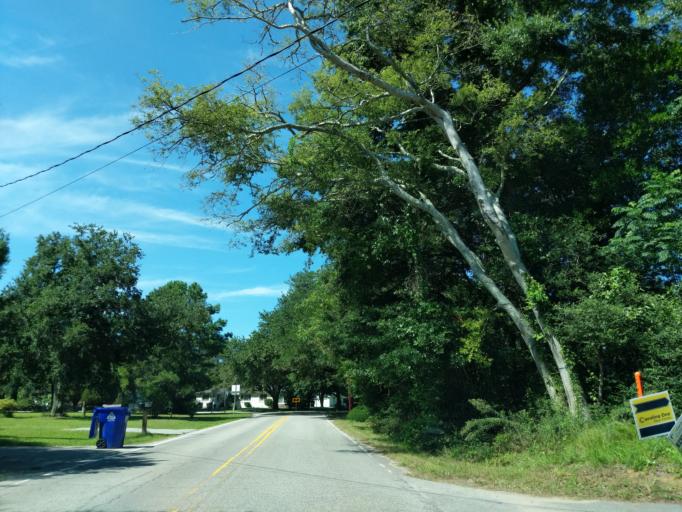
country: US
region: South Carolina
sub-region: Charleston County
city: Folly Beach
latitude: 32.7030
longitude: -79.9583
